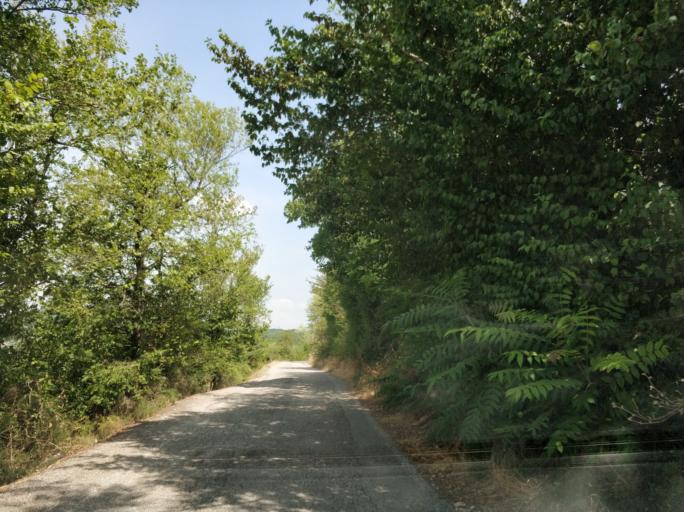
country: IT
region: Veneto
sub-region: Provincia di Padova
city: Arqua Petrarca
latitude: 45.2786
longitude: 11.7057
